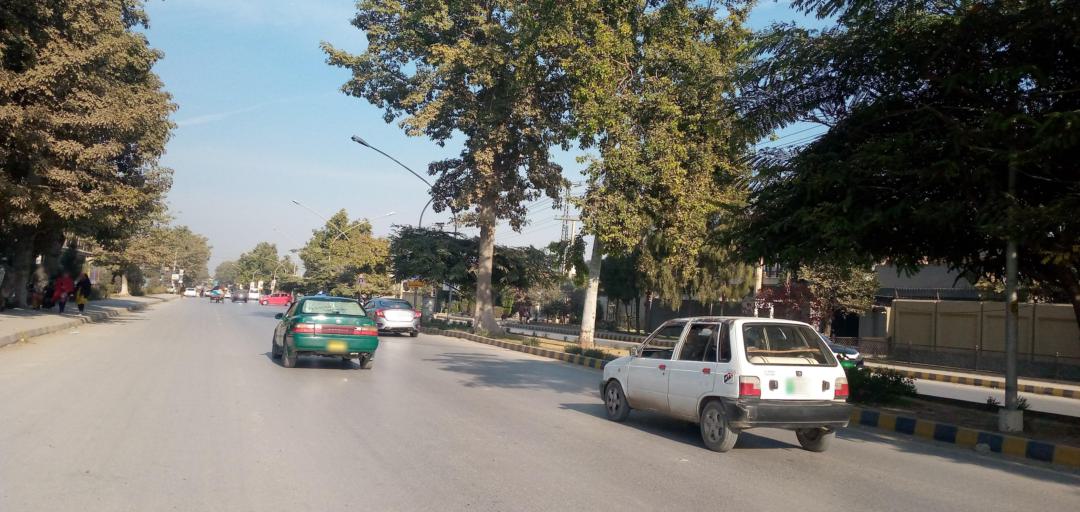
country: PK
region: Khyber Pakhtunkhwa
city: Peshawar
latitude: 33.9725
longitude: 71.4429
